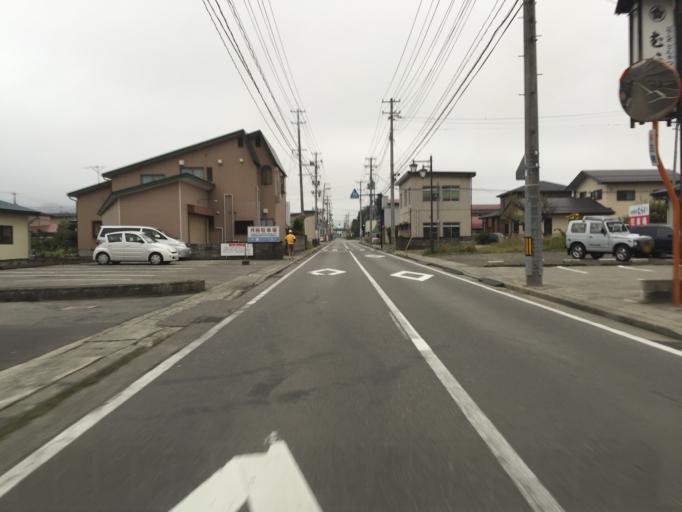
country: JP
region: Fukushima
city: Kitakata
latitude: 37.4711
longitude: 139.9236
